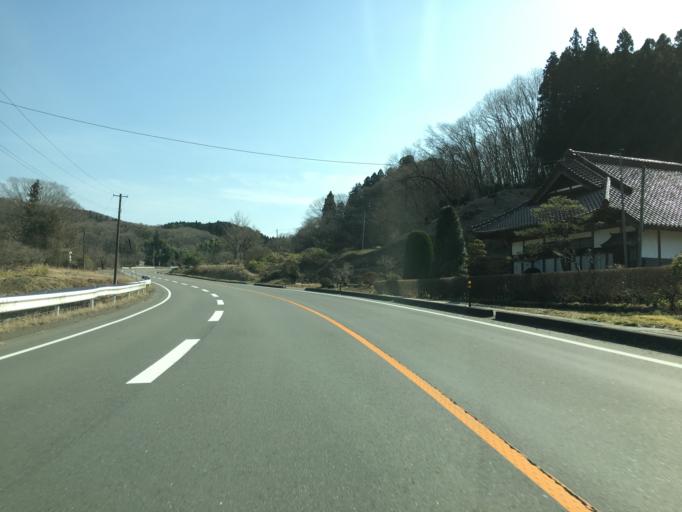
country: JP
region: Ibaraki
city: Daigo
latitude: 36.8033
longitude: 140.4703
